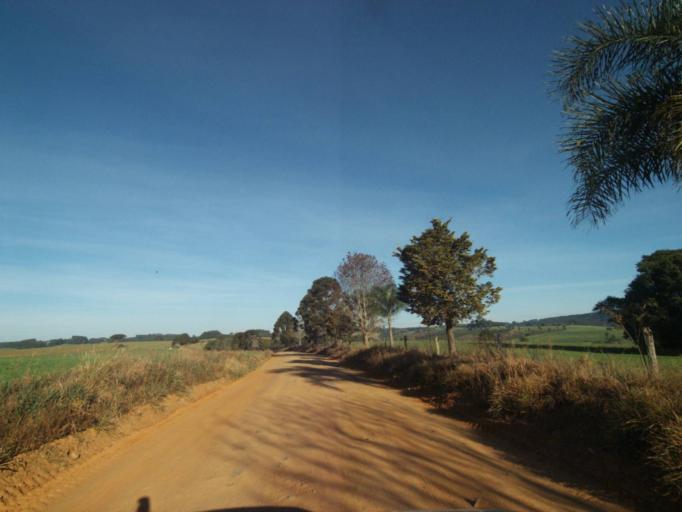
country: BR
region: Parana
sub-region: Telemaco Borba
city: Telemaco Borba
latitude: -24.5259
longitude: -50.6373
